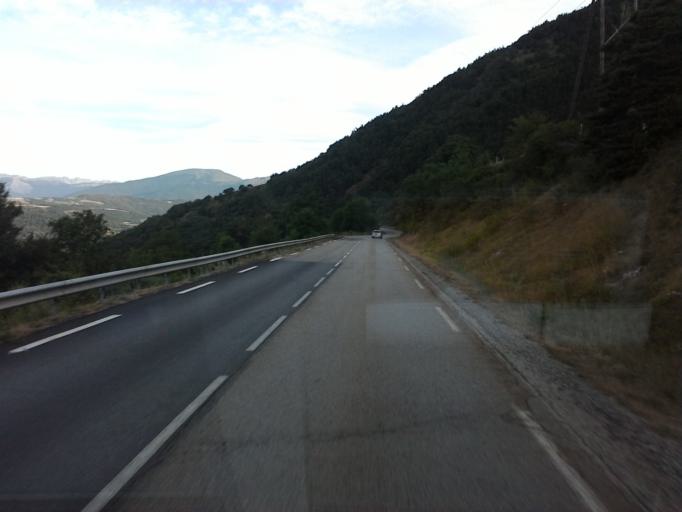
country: FR
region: Rhone-Alpes
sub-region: Departement de l'Isere
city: La Mure
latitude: 44.8419
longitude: 5.8718
